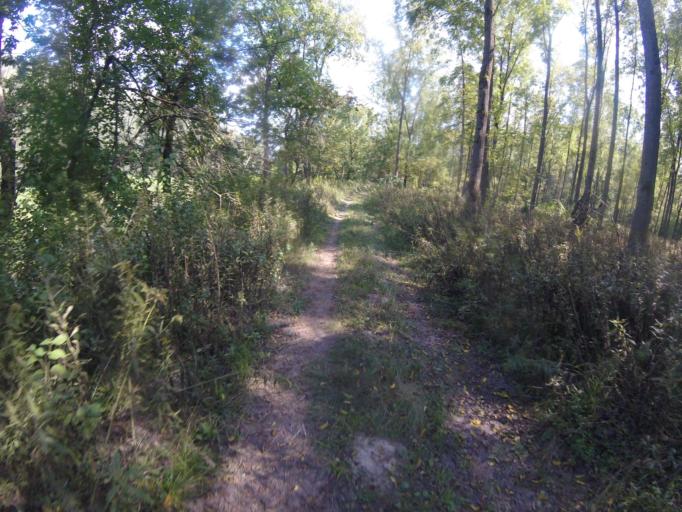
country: HU
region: Bacs-Kiskun
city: Baja
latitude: 46.1979
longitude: 18.8691
